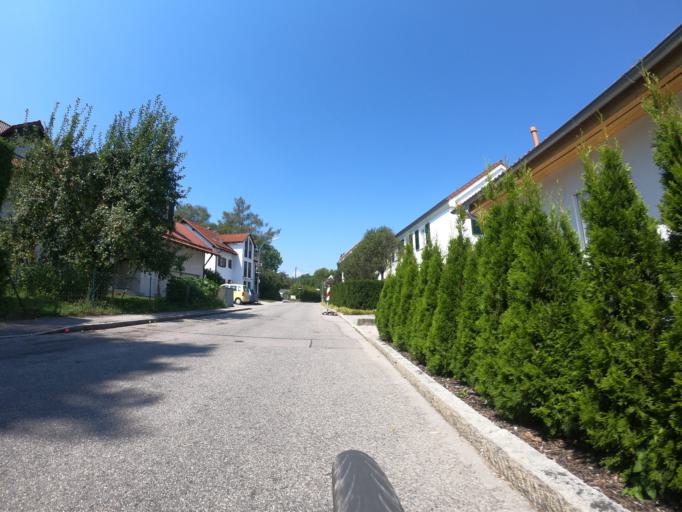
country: DE
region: Bavaria
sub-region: Upper Bavaria
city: Fuerstenfeldbruck
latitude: 48.1631
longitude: 11.2526
